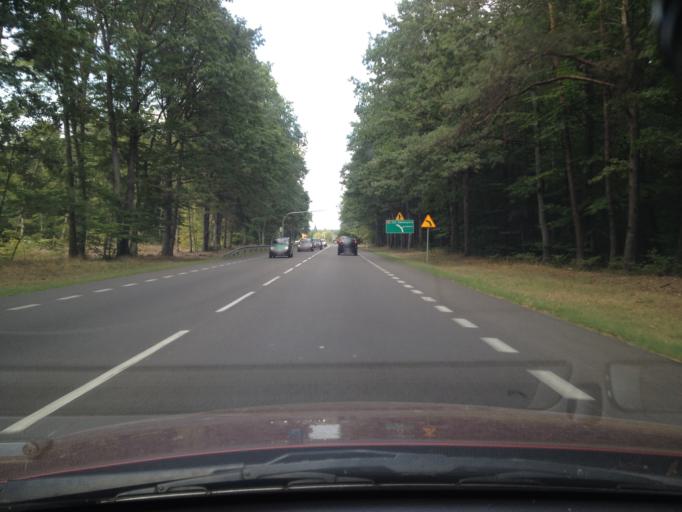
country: PL
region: West Pomeranian Voivodeship
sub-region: Powiat goleniowski
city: Przybiernow
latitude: 53.6726
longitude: 14.8139
